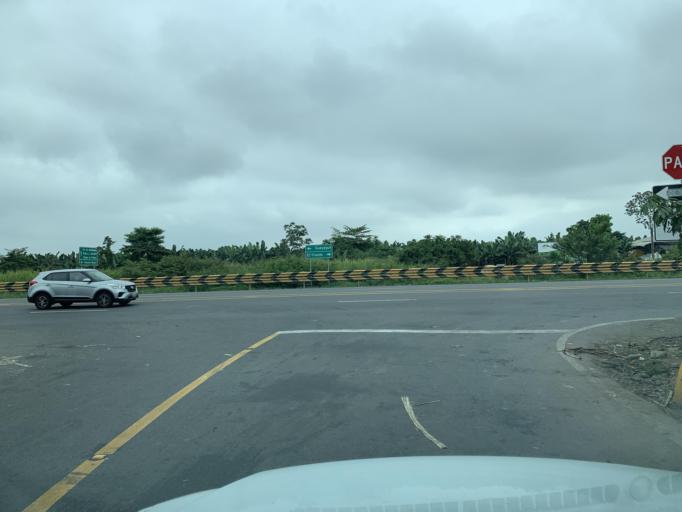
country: EC
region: Guayas
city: Coronel Marcelino Mariduena
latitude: -2.2931
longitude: -79.5019
